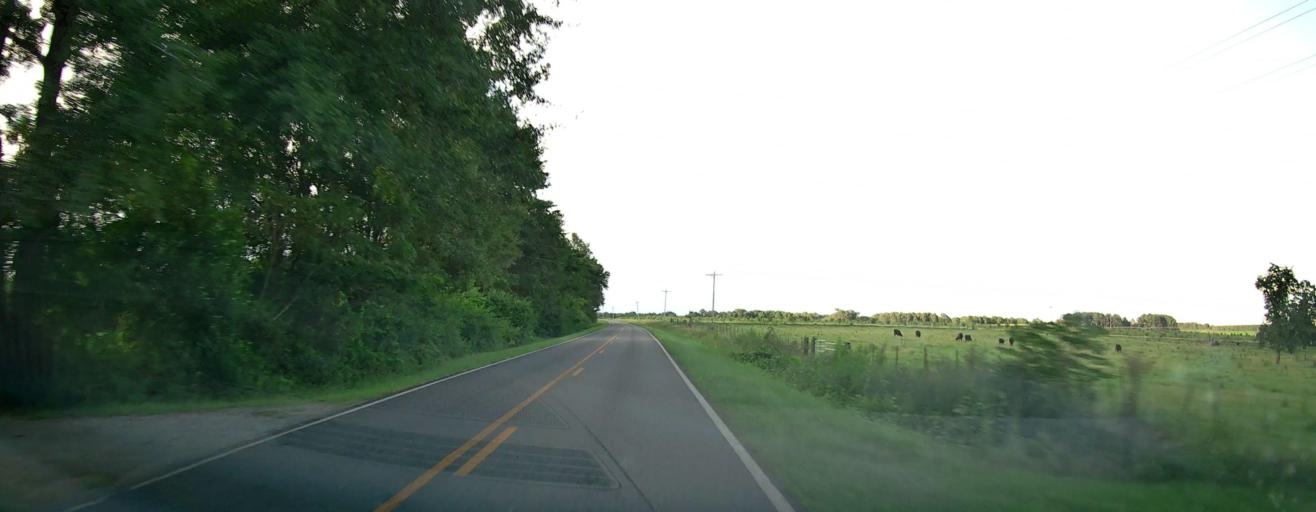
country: US
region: Georgia
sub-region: Pulaski County
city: Hawkinsville
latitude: 32.3125
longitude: -83.5527
